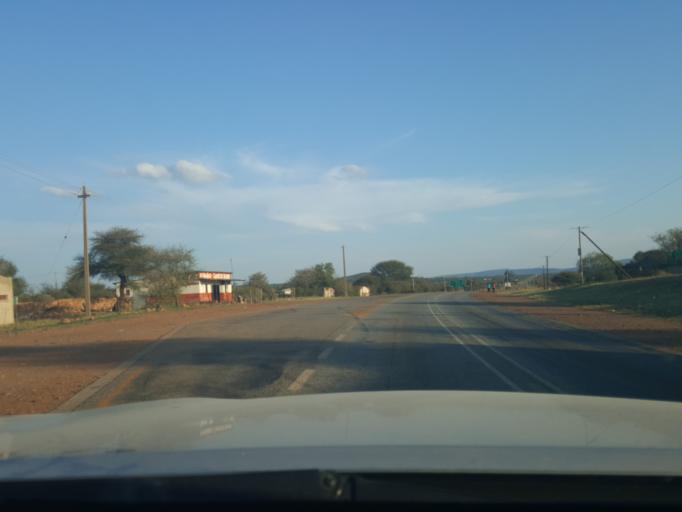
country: ZA
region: North-West
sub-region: Ngaka Modiri Molema District Municipality
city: Zeerust
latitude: -25.3864
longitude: 26.0844
